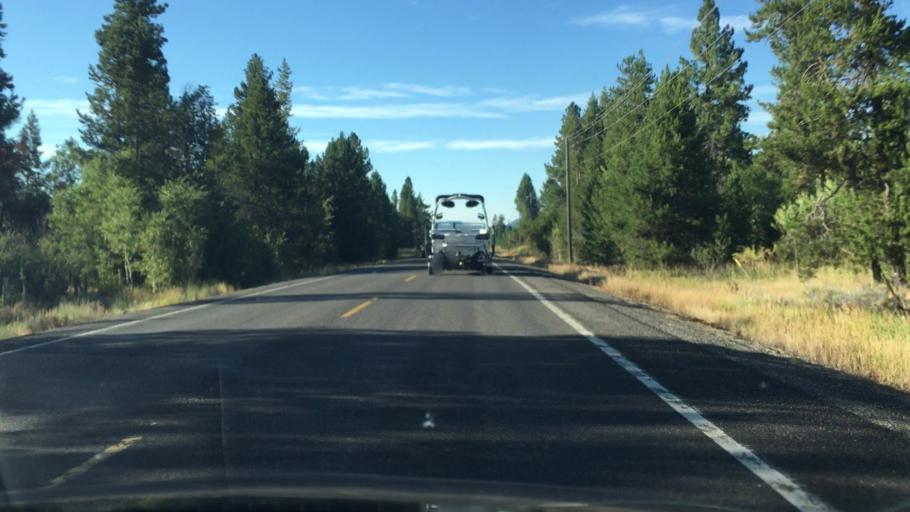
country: US
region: Idaho
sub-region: Valley County
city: Cascade
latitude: 44.4564
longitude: -115.9993
